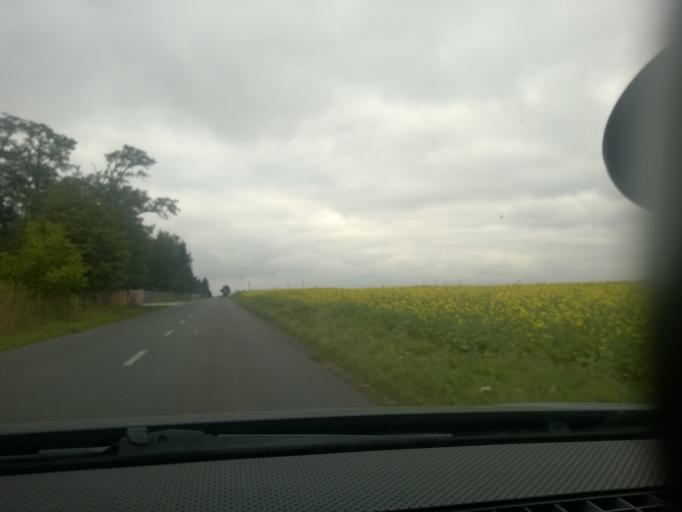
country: PL
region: Greater Poland Voivodeship
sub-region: Powiat kaliski
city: Opatowek
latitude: 51.7263
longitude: 18.1883
